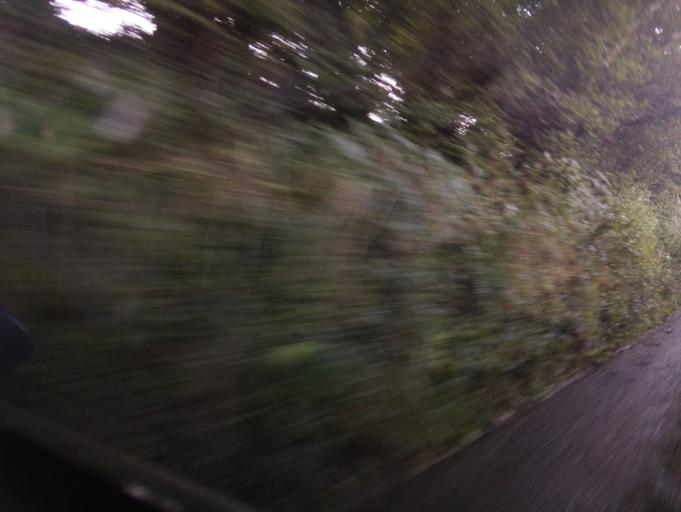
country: GB
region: England
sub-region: Devon
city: Dartmouth
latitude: 50.3393
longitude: -3.6050
